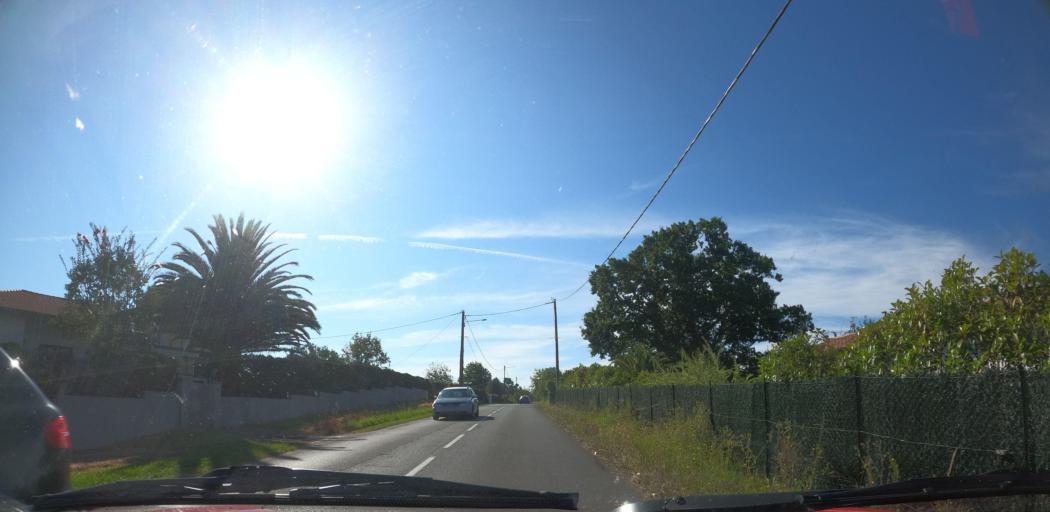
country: FR
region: Aquitaine
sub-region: Departement des Pyrenees-Atlantiques
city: Arbonne
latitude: 43.4100
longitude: -1.5462
